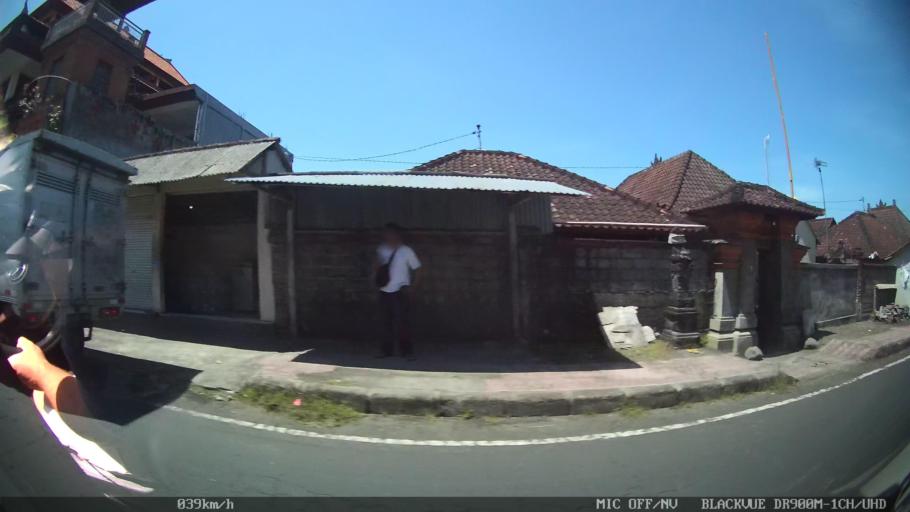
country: ID
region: Bali
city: Klungkung
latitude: -8.5739
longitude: 115.3497
